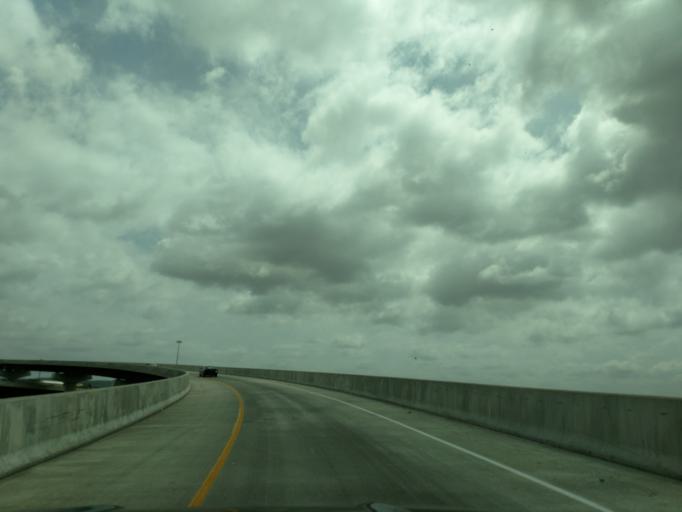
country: US
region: Nebraska
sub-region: Douglas County
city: Omaha
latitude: 41.2311
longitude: -95.8987
